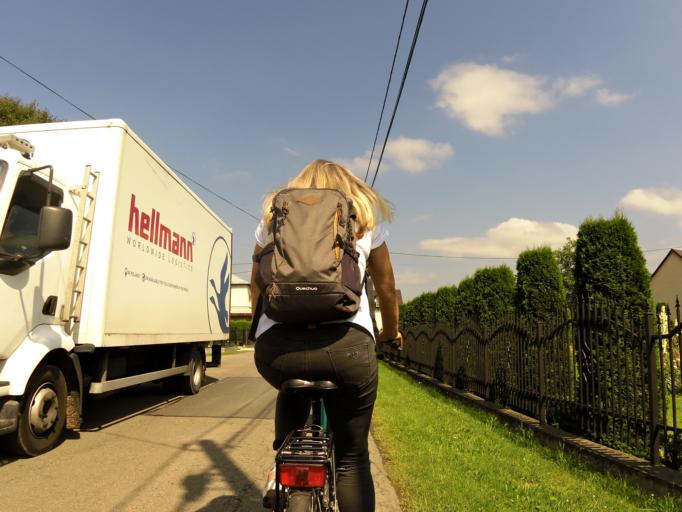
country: PL
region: Silesian Voivodeship
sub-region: Powiat zywiecki
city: Ciecina
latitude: 49.6216
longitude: 19.1486
